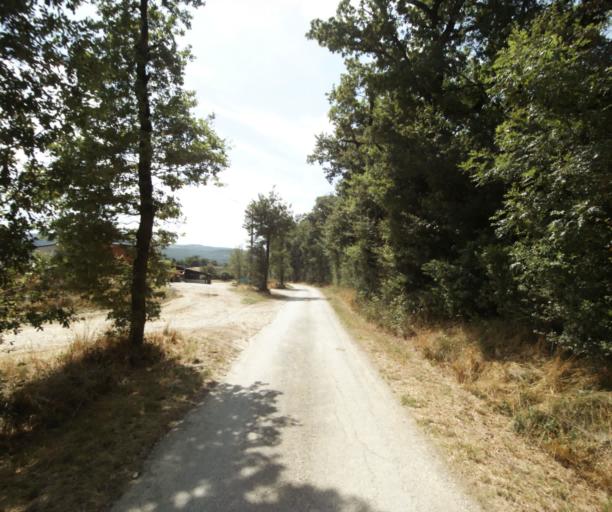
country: FR
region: Midi-Pyrenees
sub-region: Departement du Tarn
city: Dourgne
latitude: 43.4852
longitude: 2.1021
